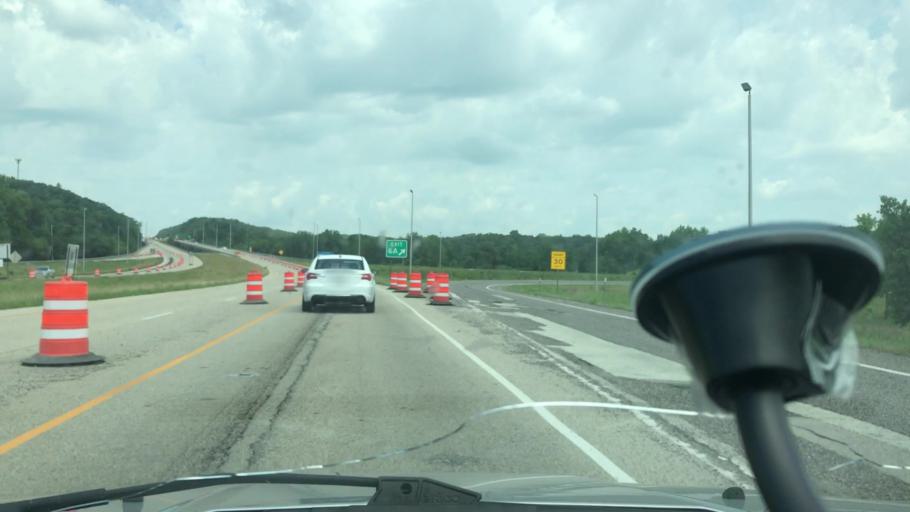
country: US
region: Illinois
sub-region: Peoria County
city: Bartonville
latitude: 40.6576
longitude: -89.6443
